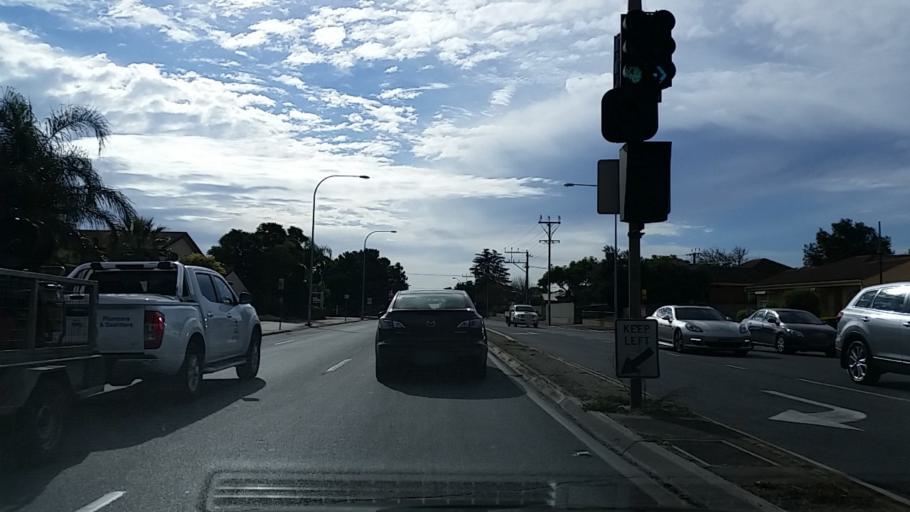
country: AU
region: South Australia
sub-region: Mitcham
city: Clarence Gardens
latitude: -34.9772
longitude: 138.5916
